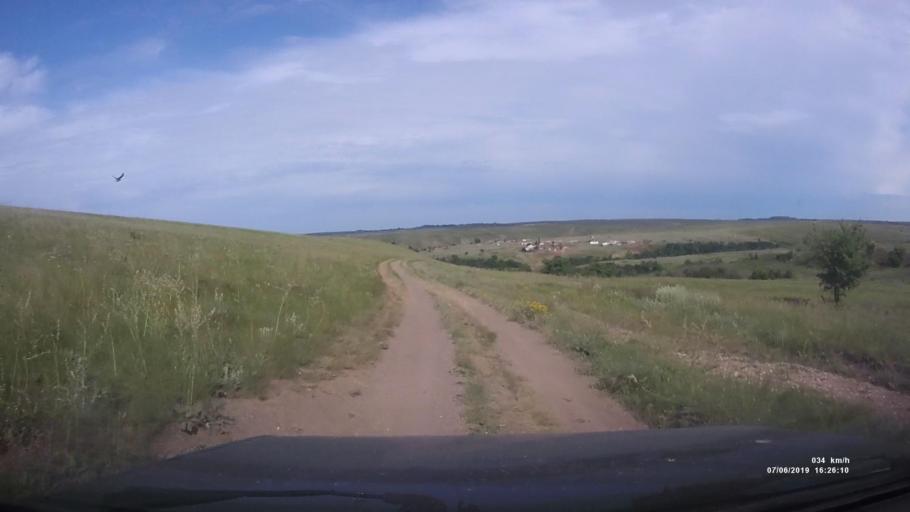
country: RU
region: Rostov
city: Kamensk-Shakhtinskiy
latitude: 48.2530
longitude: 40.3100
